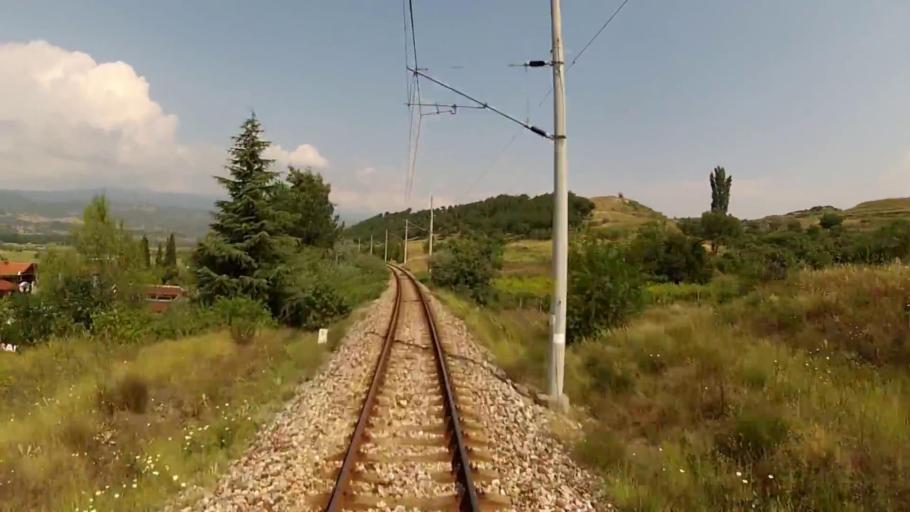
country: BG
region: Blagoevgrad
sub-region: Obshtina Strumyani
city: Strumyani
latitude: 41.6359
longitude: 23.2020
